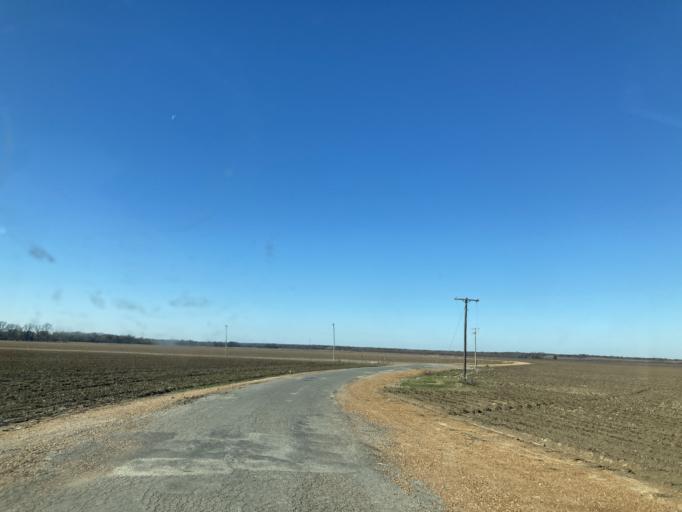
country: US
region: Mississippi
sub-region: Sharkey County
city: Rolling Fork
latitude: 32.8211
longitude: -90.7274
